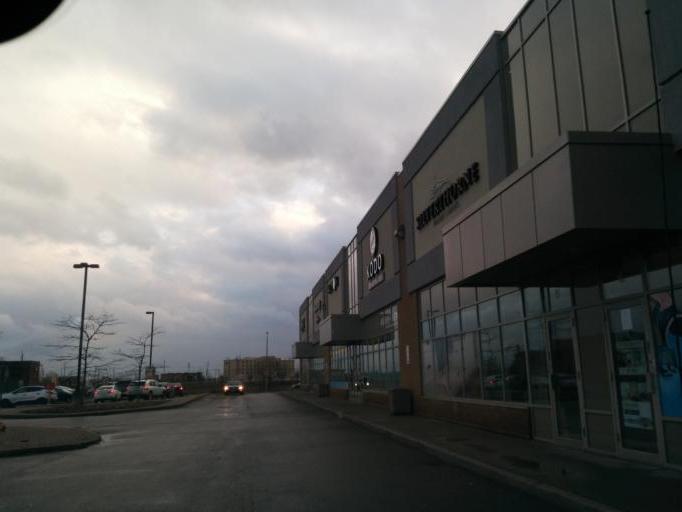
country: CA
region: Ontario
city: Etobicoke
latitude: 43.7780
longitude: -79.6240
